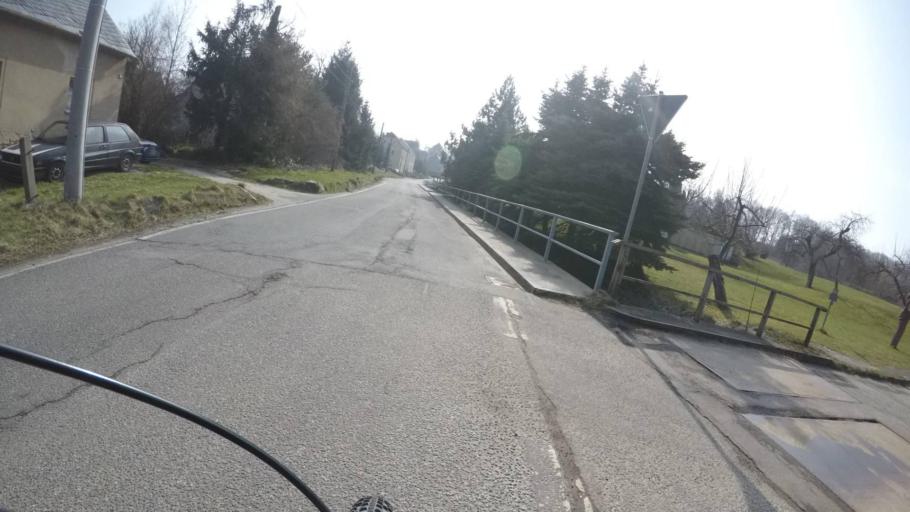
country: DE
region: Saxony
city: Niederfrohna
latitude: 50.8930
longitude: 12.6796
